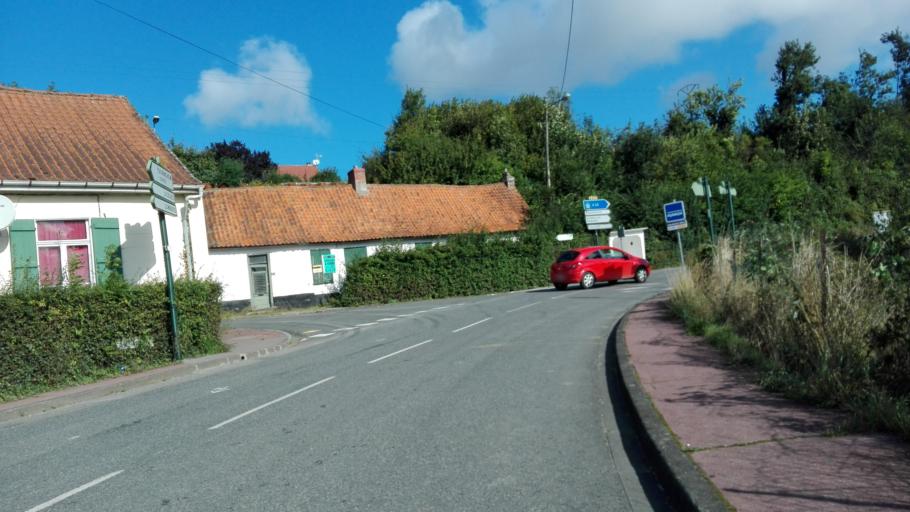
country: FR
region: Nord-Pas-de-Calais
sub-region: Departement du Pas-de-Calais
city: Tournehem-sur-la-Hem
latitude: 50.8087
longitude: 2.0459
